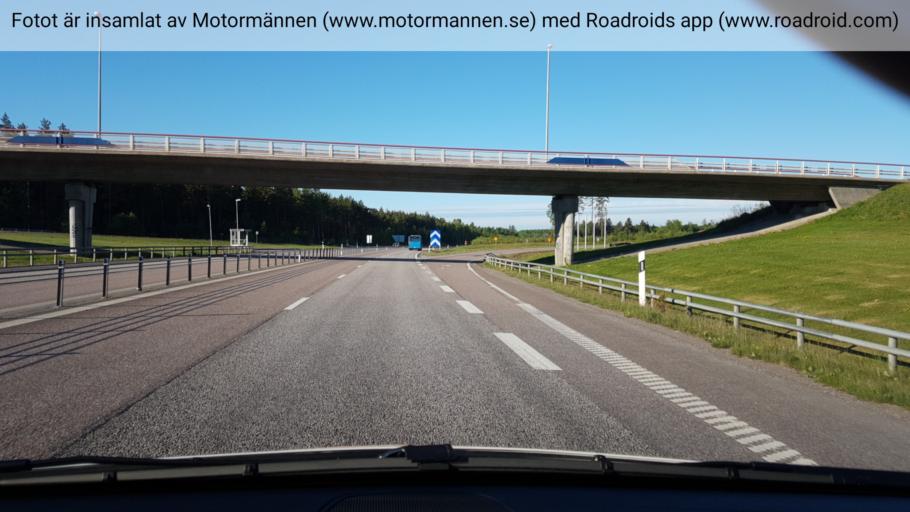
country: SE
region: Vaestra Goetaland
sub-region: Skovde Kommun
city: Skultorp
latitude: 58.3413
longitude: 13.8636
